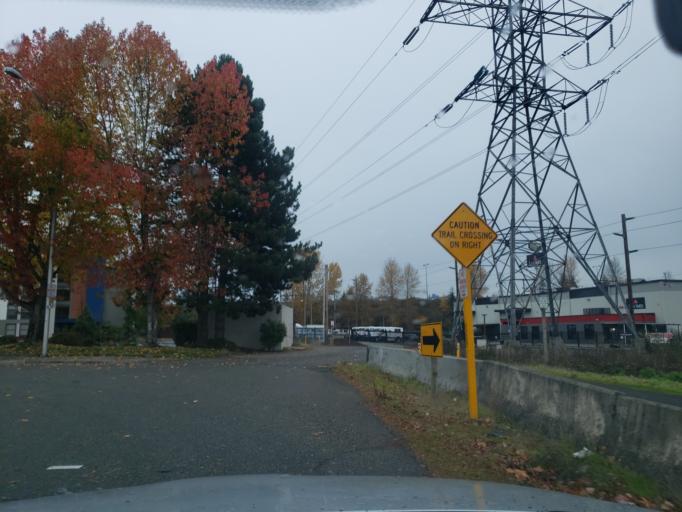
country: US
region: Washington
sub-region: King County
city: Tukwila
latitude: 47.4625
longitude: -122.2435
